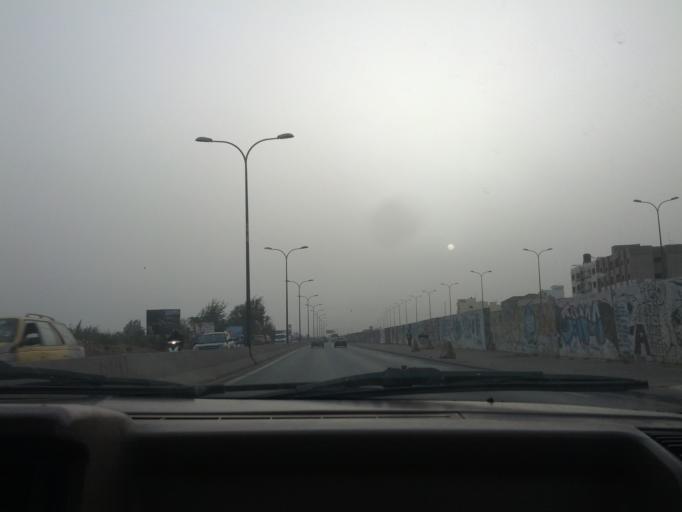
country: SN
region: Dakar
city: Grand Dakar
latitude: 14.7439
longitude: -17.4295
